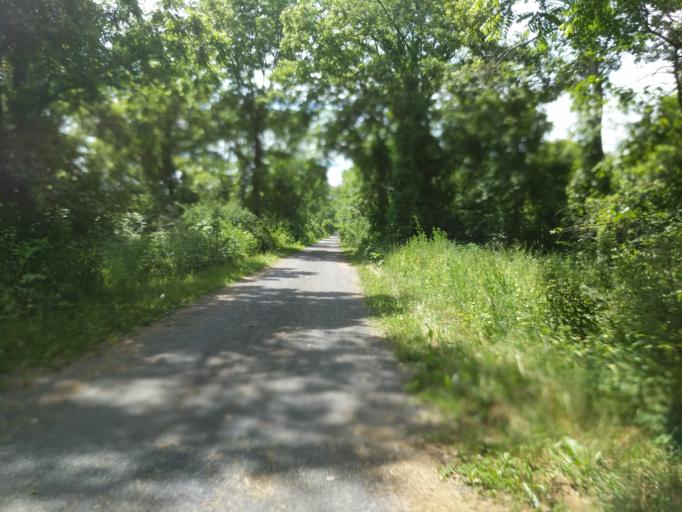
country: US
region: New York
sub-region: Tompkins County
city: Trumansburg
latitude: 42.5277
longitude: -76.5932
